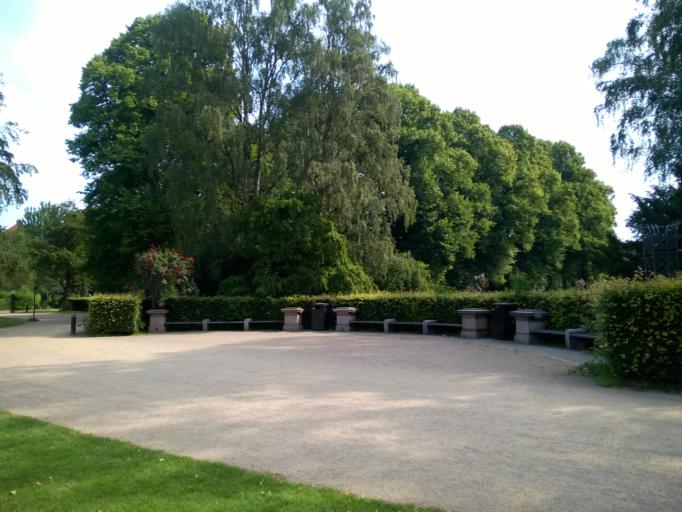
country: DK
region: Capital Region
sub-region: Kobenhavn
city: Copenhagen
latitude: 55.6990
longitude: 12.5726
